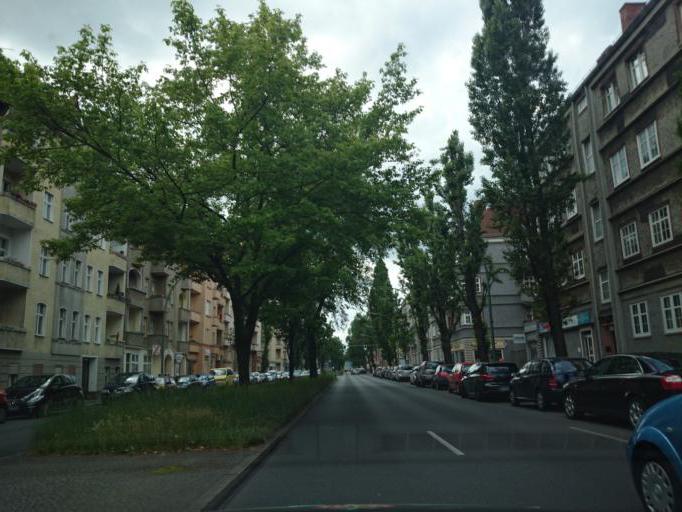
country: DE
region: Berlin
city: Tempelhof Bezirk
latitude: 52.4627
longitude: 13.3770
